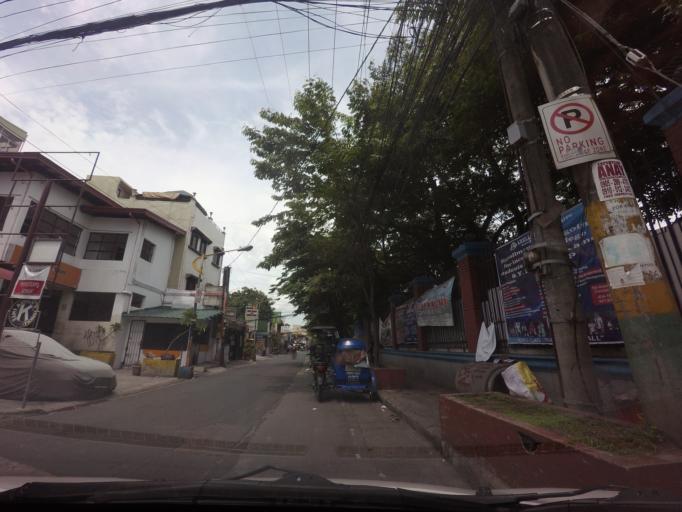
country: PH
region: Metro Manila
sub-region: Pasig
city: Pasig City
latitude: 14.5735
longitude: 121.0793
